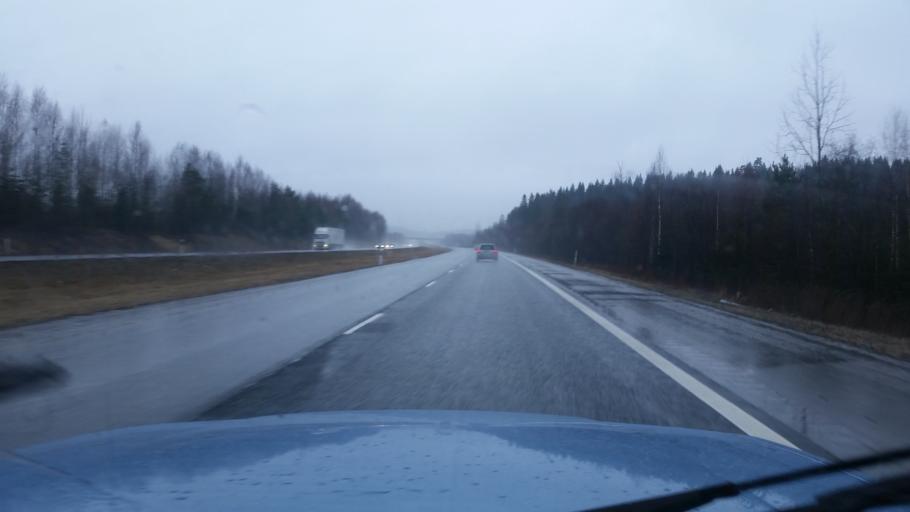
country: FI
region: Haeme
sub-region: Haemeenlinna
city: Tervakoski
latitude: 60.8384
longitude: 24.6438
